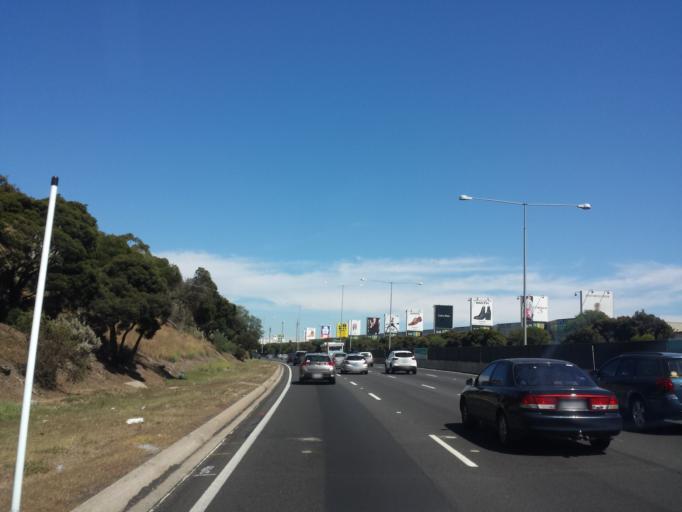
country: AU
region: Victoria
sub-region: Moonee Valley
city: Essendon North
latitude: -37.7328
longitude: 144.9129
